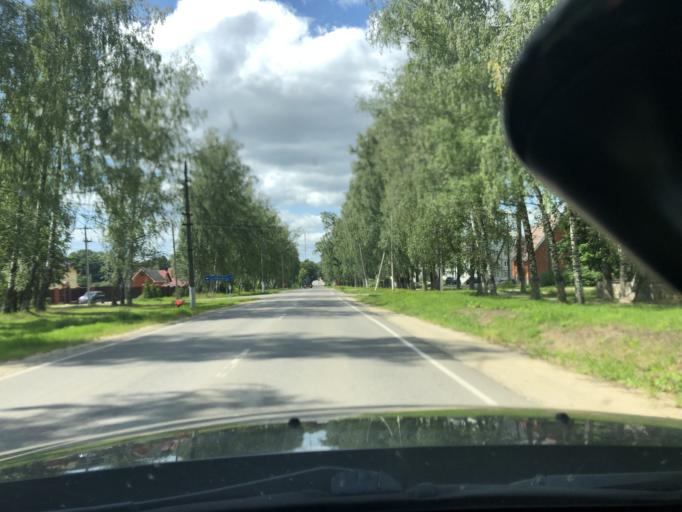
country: RU
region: Tula
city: Gorelki
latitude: 54.3372
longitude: 37.5588
